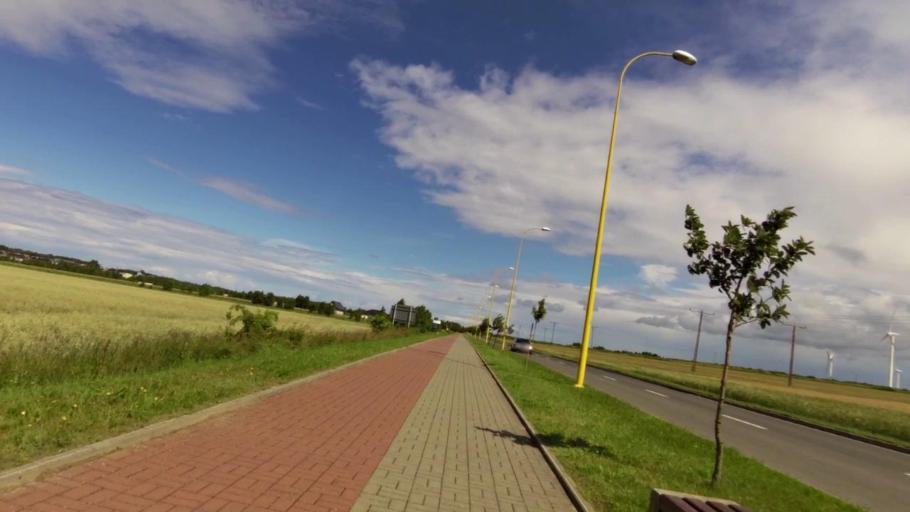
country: PL
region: West Pomeranian Voivodeship
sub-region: Powiat slawienski
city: Darlowo
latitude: 54.4382
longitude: 16.4085
